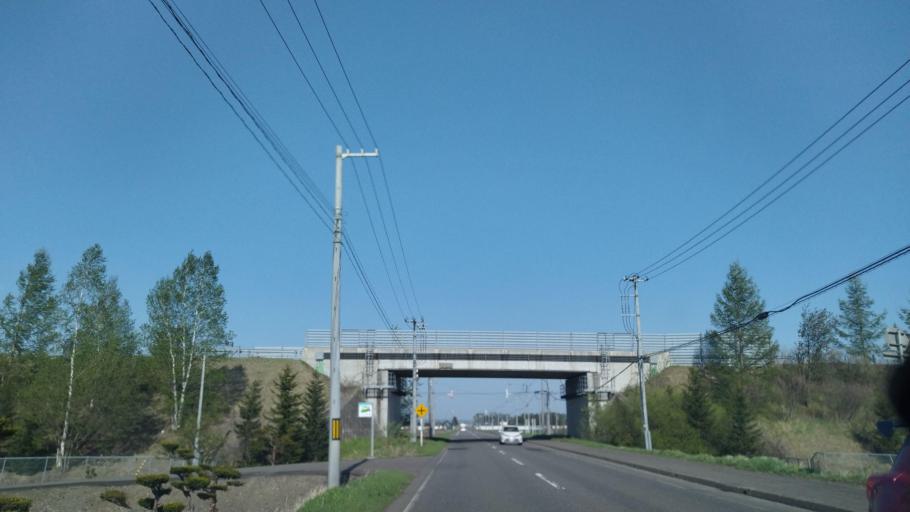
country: JP
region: Hokkaido
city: Obihiro
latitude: 42.9450
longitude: 143.1051
